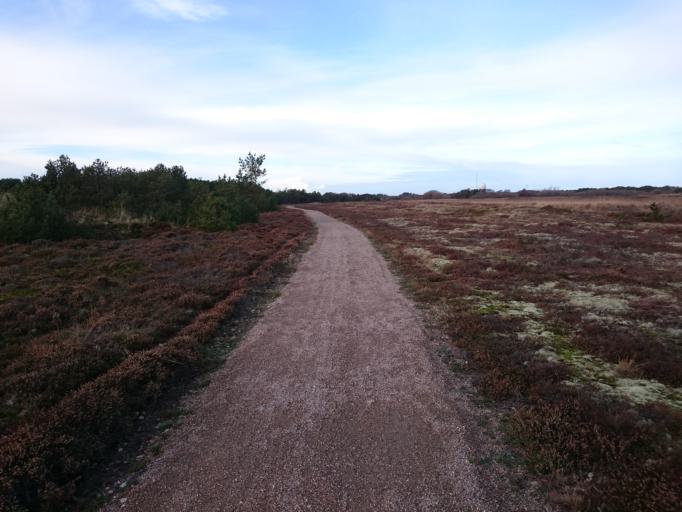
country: DK
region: North Denmark
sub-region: Frederikshavn Kommune
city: Skagen
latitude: 57.7366
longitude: 10.6213
